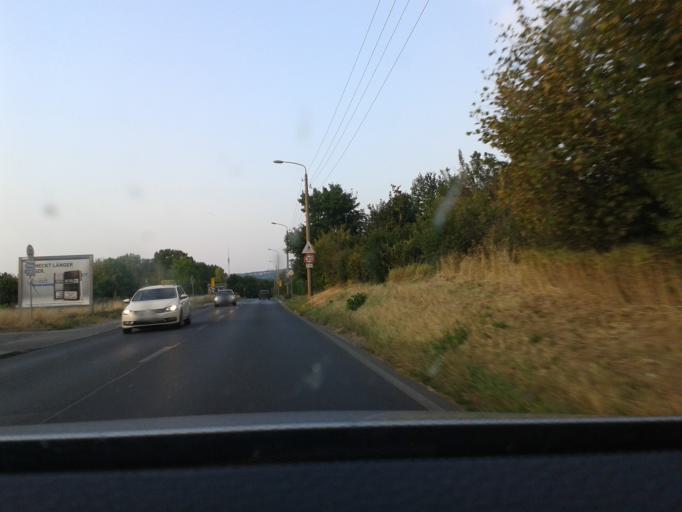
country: DE
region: Saxony
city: Heidenau
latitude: 51.0005
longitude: 13.8017
